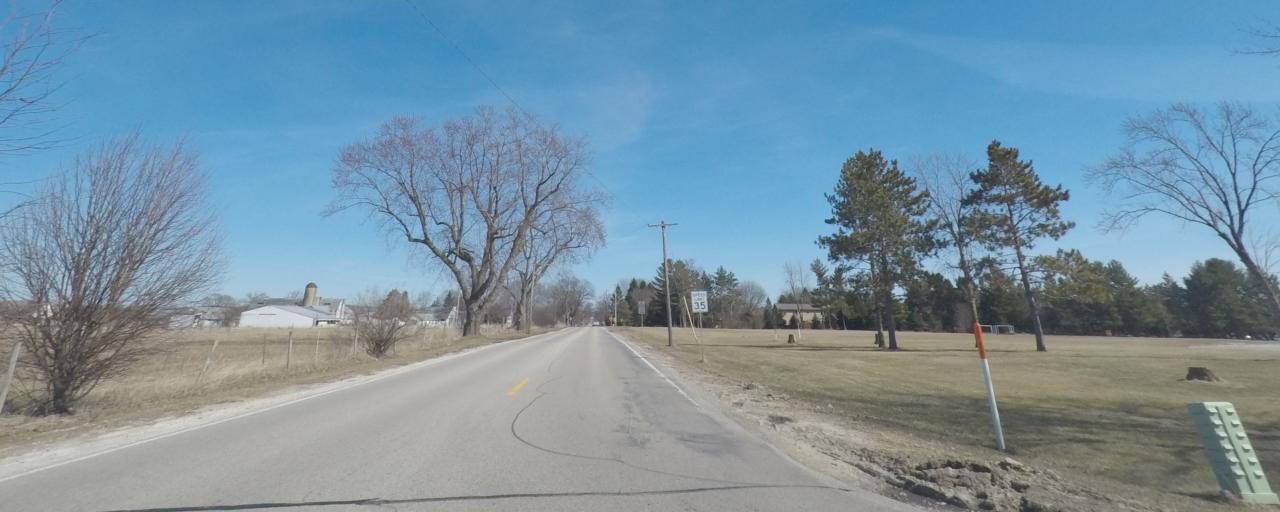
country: US
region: Wisconsin
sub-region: Waukesha County
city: Hartland
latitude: 43.1199
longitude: -88.3473
